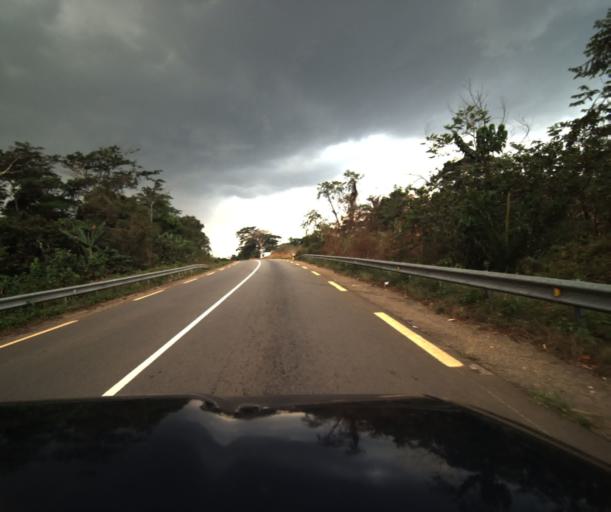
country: CM
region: Centre
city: Mbankomo
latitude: 3.6770
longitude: 11.3509
